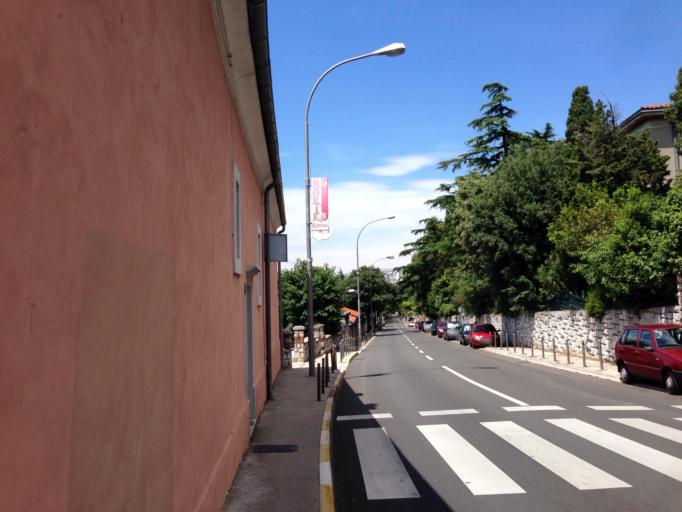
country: HR
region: Primorsko-Goranska
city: Cavle
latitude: 45.3152
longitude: 14.4708
